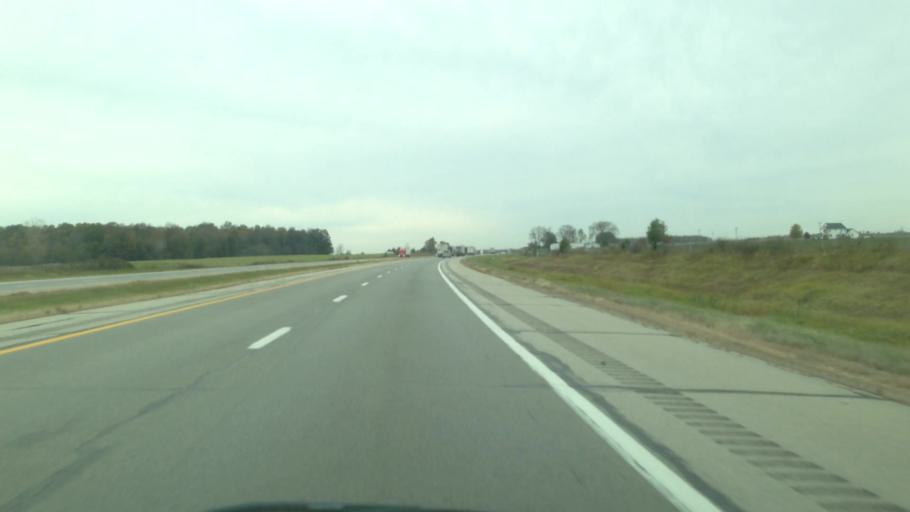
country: US
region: Ohio
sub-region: Williams County
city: Montpelier
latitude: 41.6187
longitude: -84.6775
